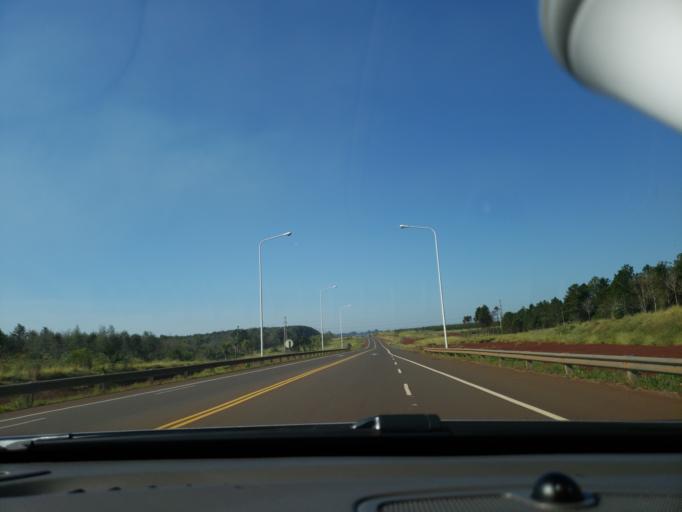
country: AR
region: Misiones
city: Garupa
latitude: -27.4656
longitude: -55.9164
